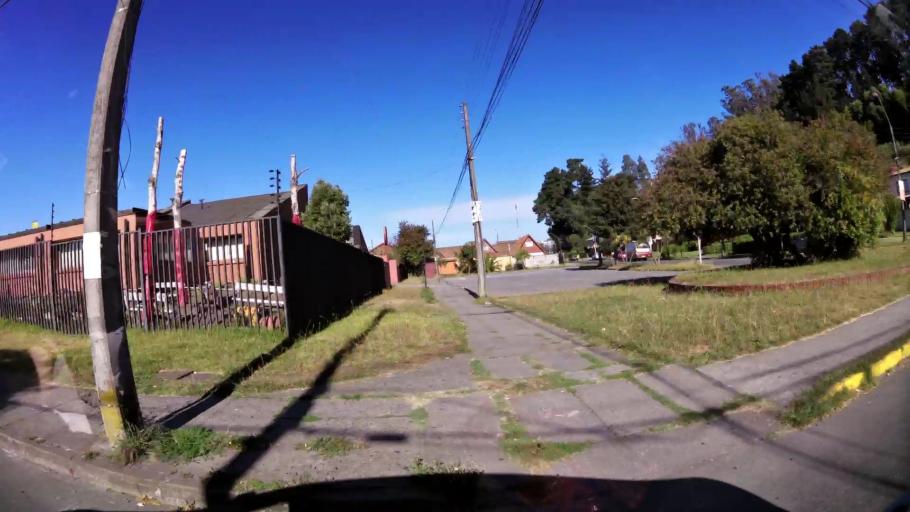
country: CL
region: Biobio
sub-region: Provincia de Concepcion
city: Concepcion
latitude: -36.8428
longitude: -73.1075
